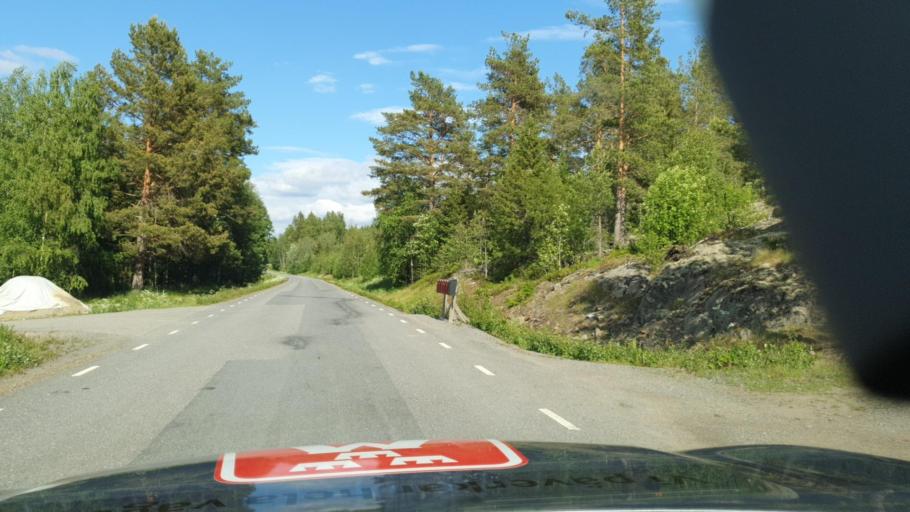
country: SE
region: Vaesternorrland
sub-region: Haernoesands Kommun
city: Haernoesand
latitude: 62.8079
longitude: 18.0991
